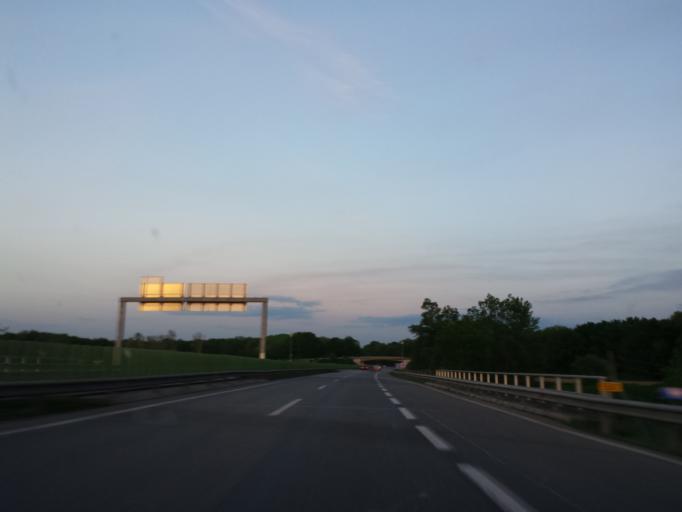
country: AT
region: Lower Austria
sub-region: Politischer Bezirk Tulln
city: Tulln
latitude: 48.3624
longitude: 16.0654
